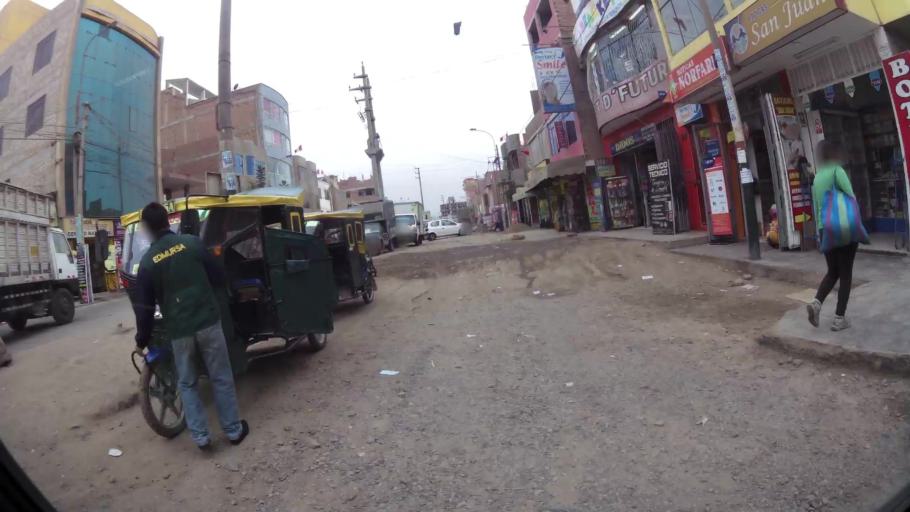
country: PE
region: Lima
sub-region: Lima
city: Independencia
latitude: -11.9667
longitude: -77.0904
